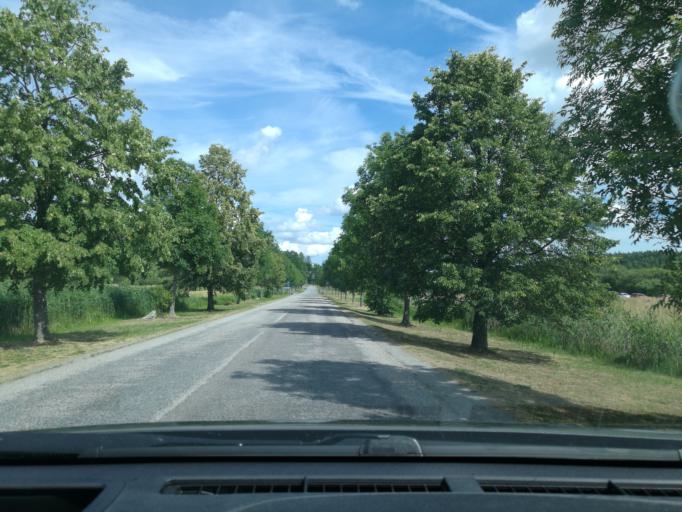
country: SE
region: Stockholm
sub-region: Sigtuna Kommun
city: Marsta
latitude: 59.6043
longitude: 17.8123
